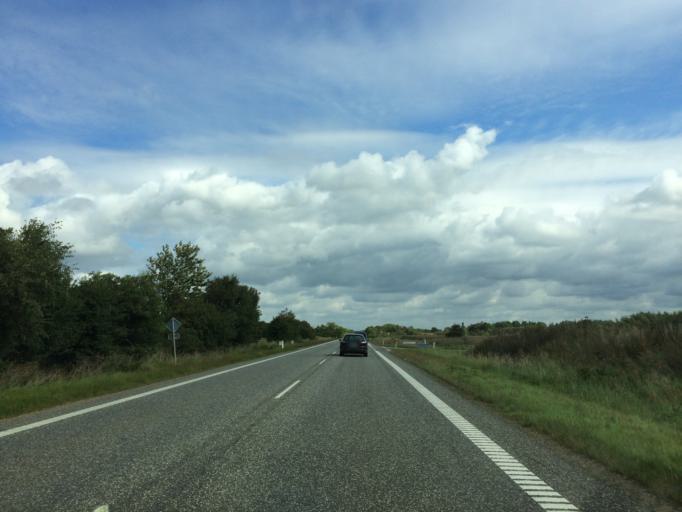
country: DK
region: Central Jutland
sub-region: Holstebro Kommune
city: Vinderup
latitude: 56.3797
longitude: 8.7661
